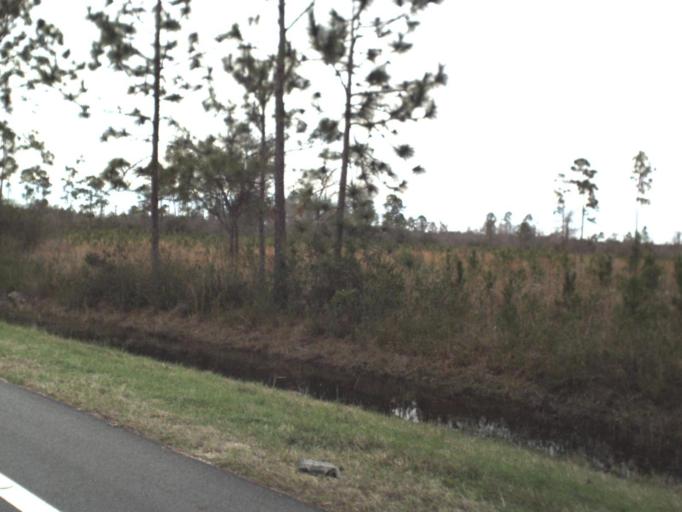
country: US
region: Florida
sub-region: Gulf County
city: Wewahitchka
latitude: 30.1387
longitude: -85.2492
